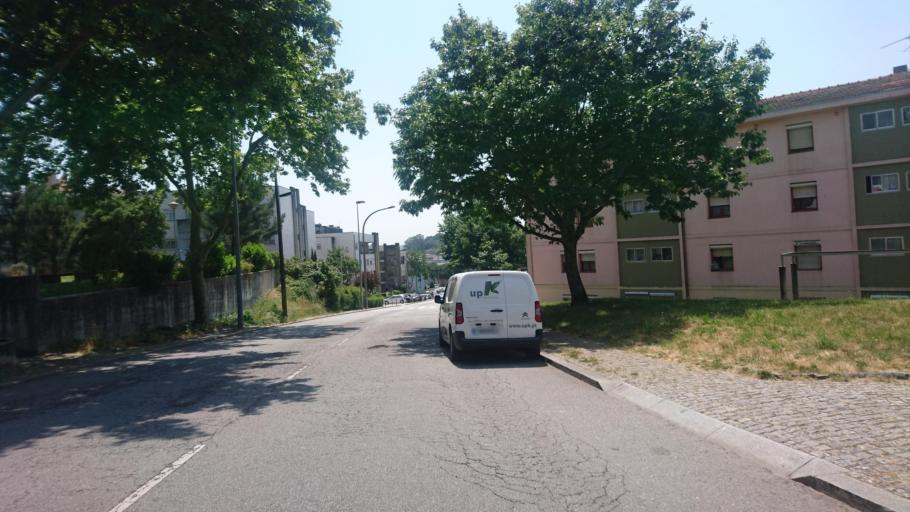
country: PT
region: Porto
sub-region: Gondomar
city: Rio Tinto
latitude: 41.1604
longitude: -8.5677
